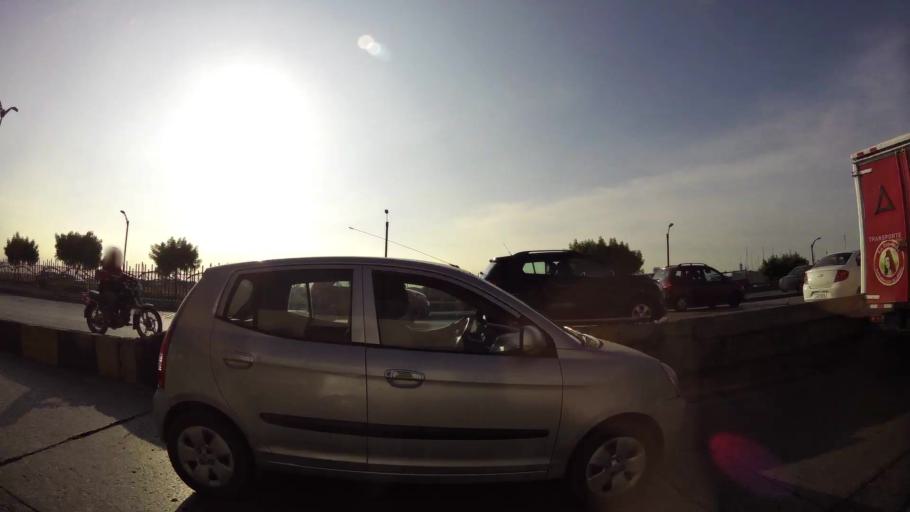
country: EC
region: Guayas
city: Eloy Alfaro
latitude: -2.1699
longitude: -79.8920
